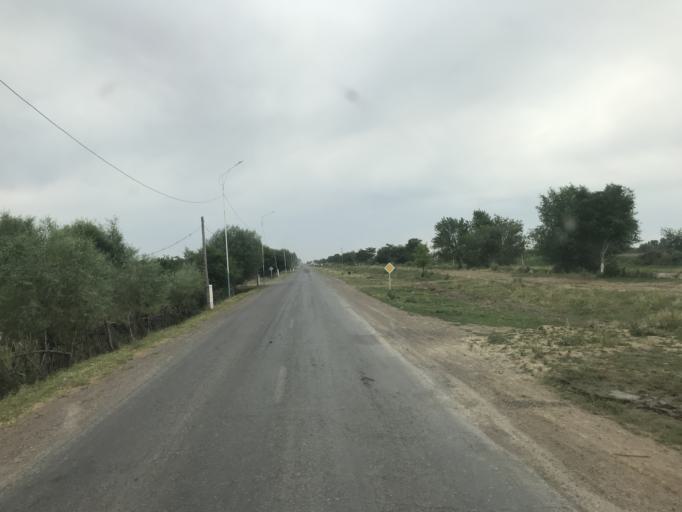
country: KZ
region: Ongtustik Qazaqstan
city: Asykata
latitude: 40.9417
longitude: 68.4150
